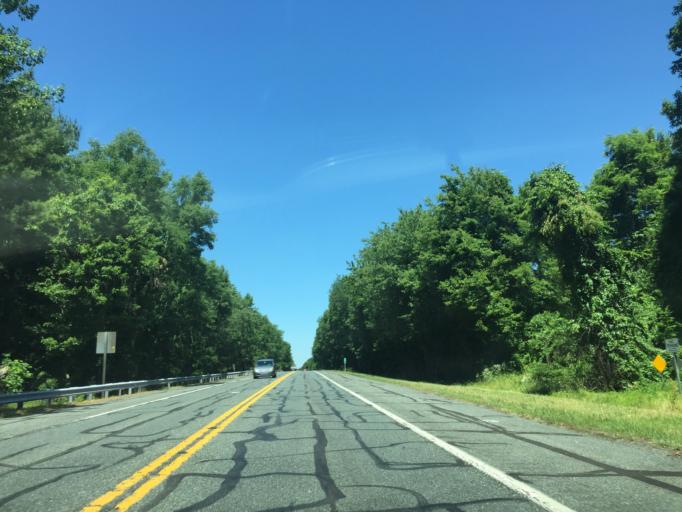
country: US
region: Maryland
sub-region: Harford County
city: Jarrettsville
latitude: 39.5791
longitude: -76.4464
